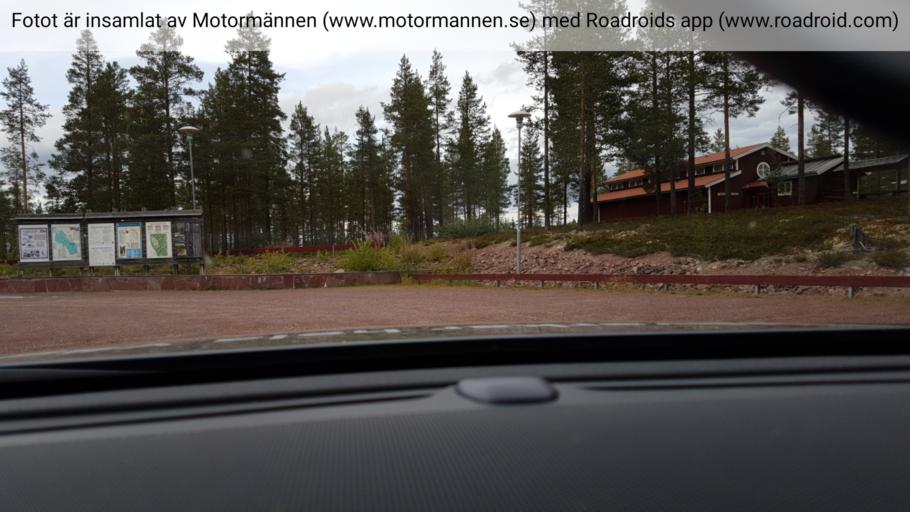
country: NO
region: Hedmark
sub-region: Trysil
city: Innbygda
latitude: 61.6938
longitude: 13.0762
